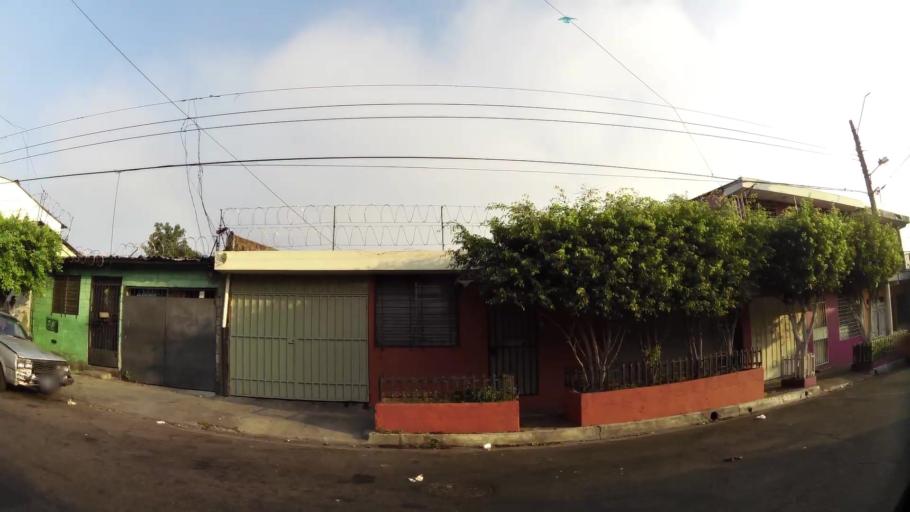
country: SV
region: San Salvador
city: San Salvador
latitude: 13.6896
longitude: -89.1994
